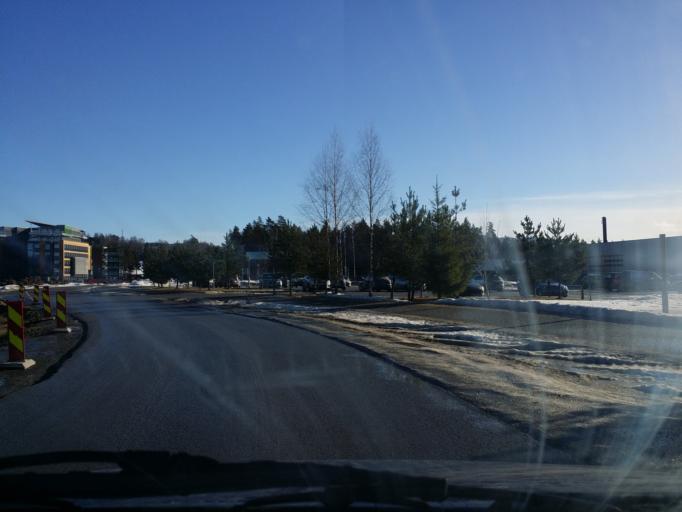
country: NO
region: Buskerud
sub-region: Ringerike
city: Honefoss
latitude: 60.1455
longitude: 10.2502
